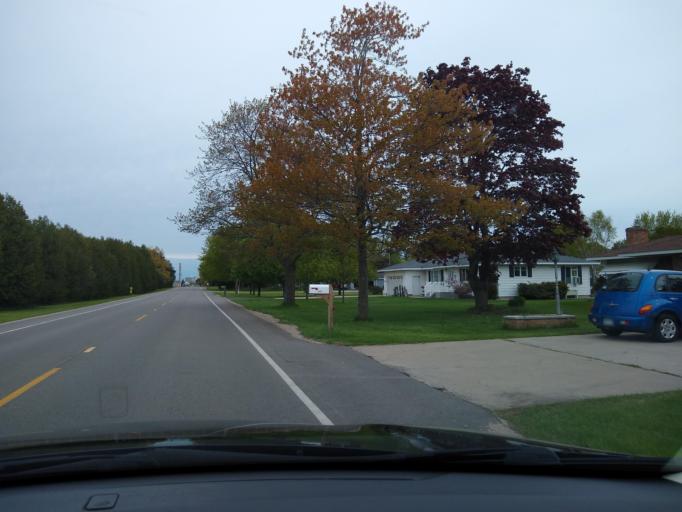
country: US
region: Michigan
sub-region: Delta County
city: Escanaba
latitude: 45.7855
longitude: -87.0778
